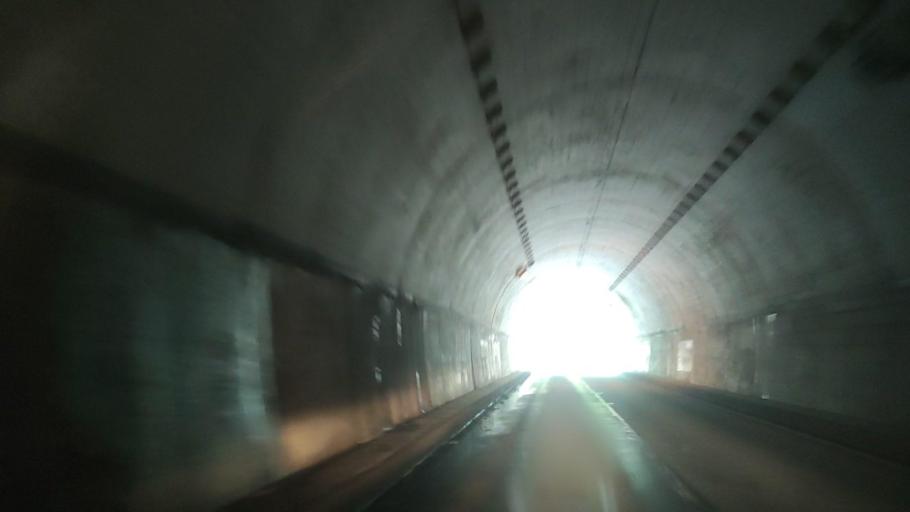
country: JP
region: Hyogo
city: Toyooka
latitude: 35.6378
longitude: 134.7760
